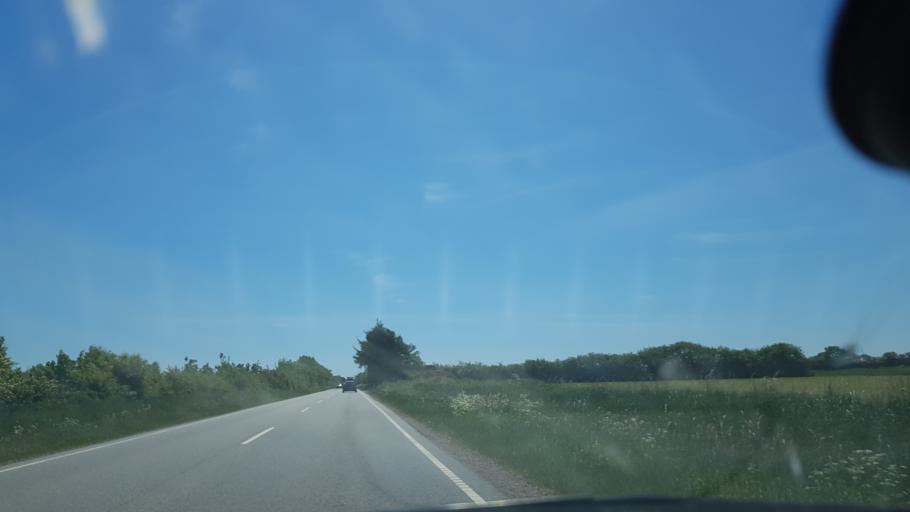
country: DK
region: South Denmark
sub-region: Tonder Kommune
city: Sherrebek
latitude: 55.0836
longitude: 8.8230
